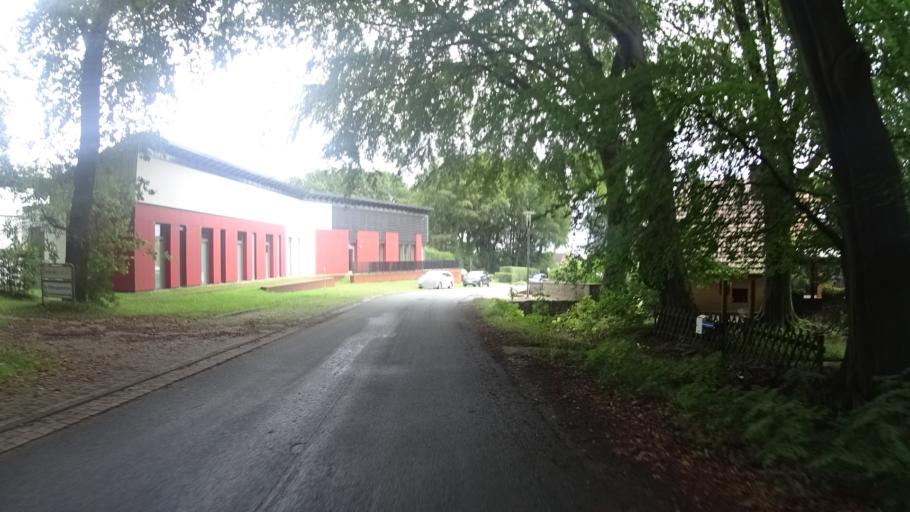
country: DE
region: Lower Saxony
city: Lintig
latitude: 53.6157
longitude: 8.8435
